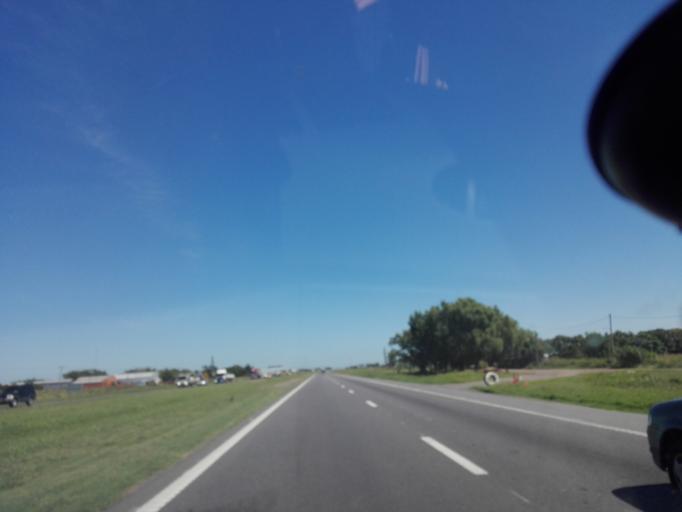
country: AR
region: Buenos Aires
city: San Nicolas de los Arroyos
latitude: -33.3820
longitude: -60.2308
